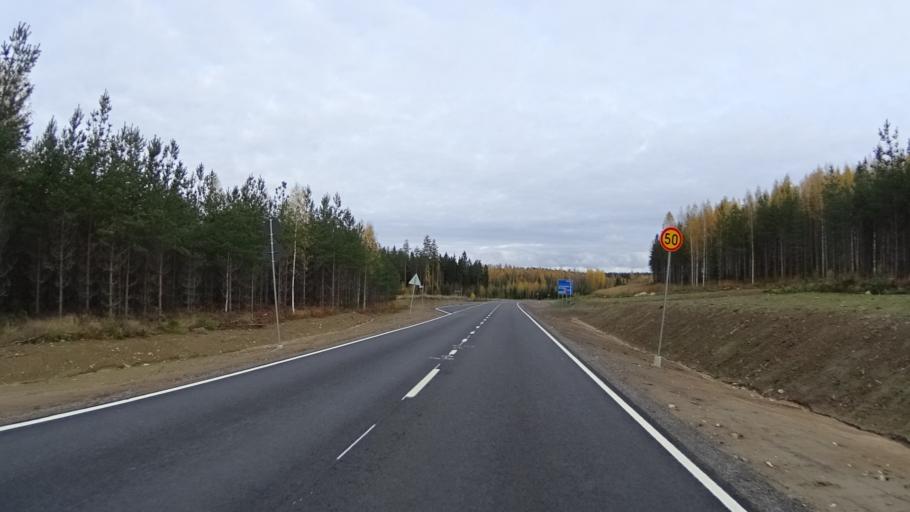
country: FI
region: South Karelia
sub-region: Lappeenranta
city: Taipalsaari
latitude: 61.0284
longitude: 28.0313
